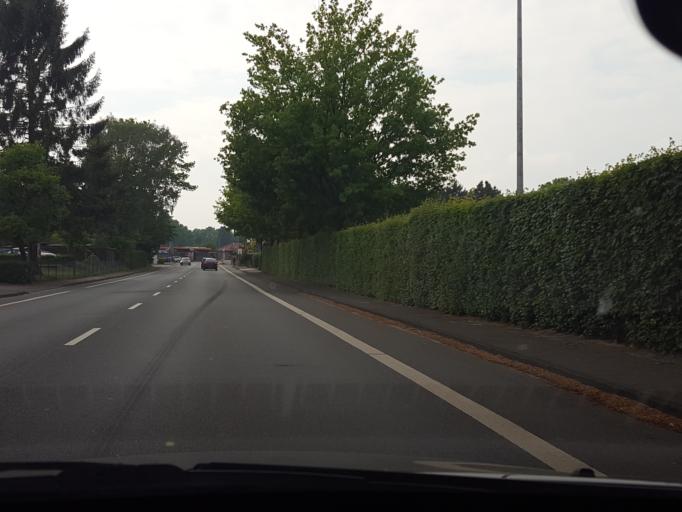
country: DE
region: North Rhine-Westphalia
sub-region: Regierungsbezirk Munster
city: Sudlohn
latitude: 51.9365
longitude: 6.7988
